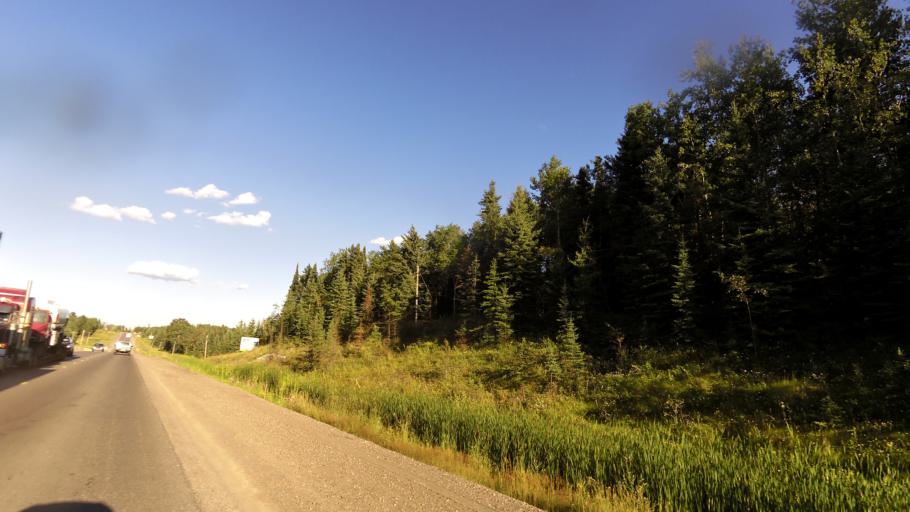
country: CA
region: Ontario
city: Dryden
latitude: 49.8151
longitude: -92.8636
